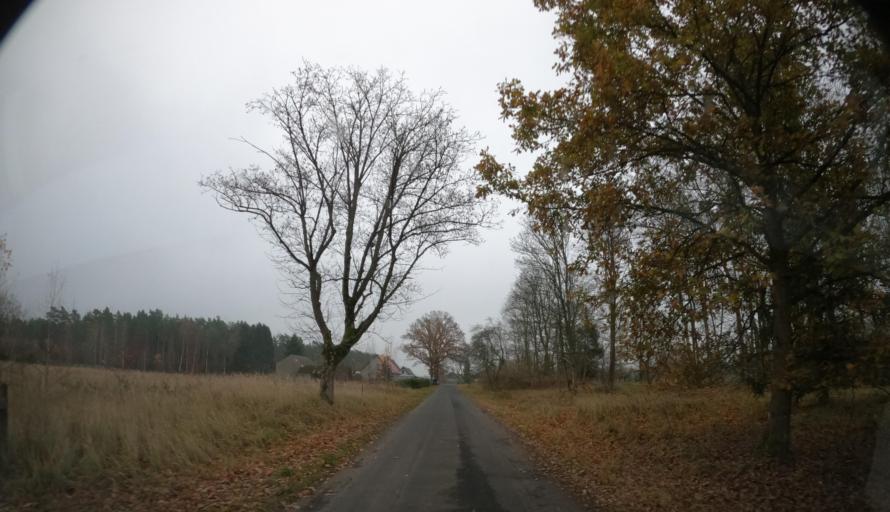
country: PL
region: West Pomeranian Voivodeship
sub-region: Powiat lobeski
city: Radowo Male
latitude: 53.6811
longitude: 15.4653
